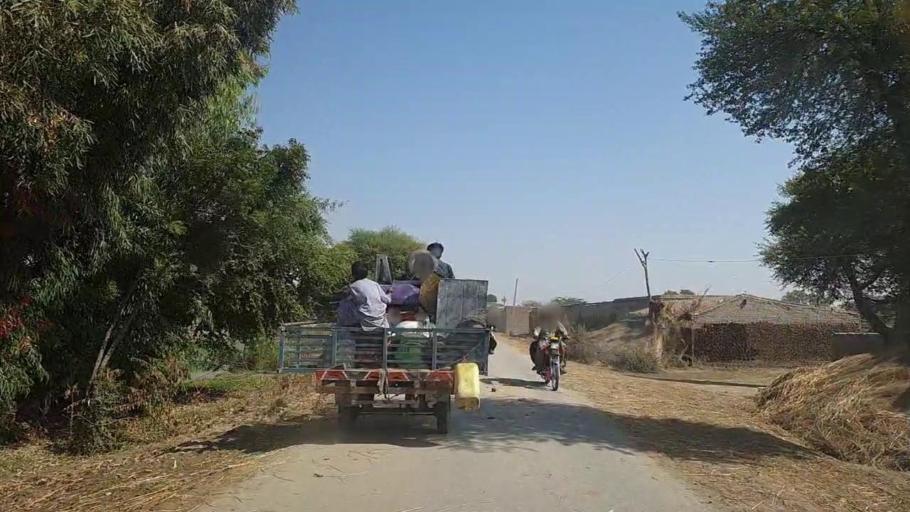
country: PK
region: Sindh
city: Thul
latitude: 28.2446
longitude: 68.8029
